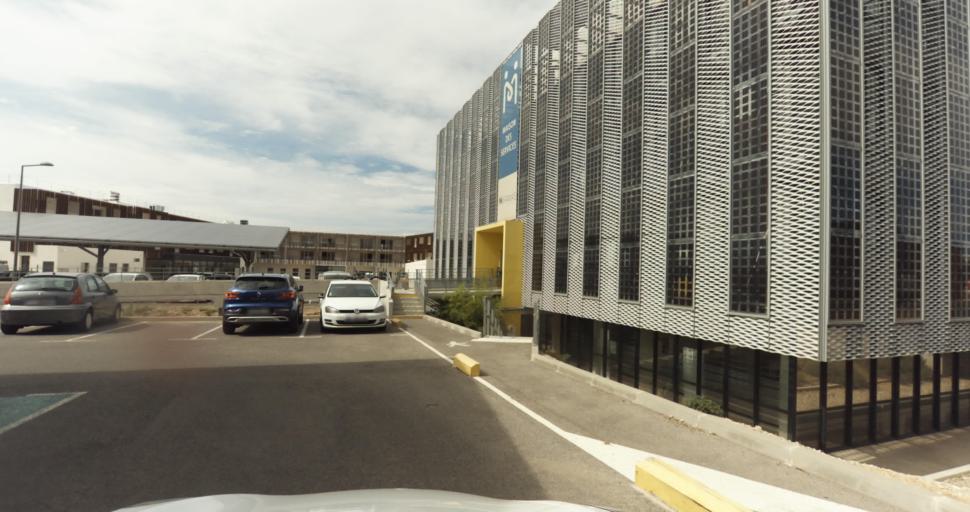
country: FR
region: Provence-Alpes-Cote d'Azur
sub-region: Departement des Bouches-du-Rhone
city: Miramas
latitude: 43.5755
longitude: 4.9978
